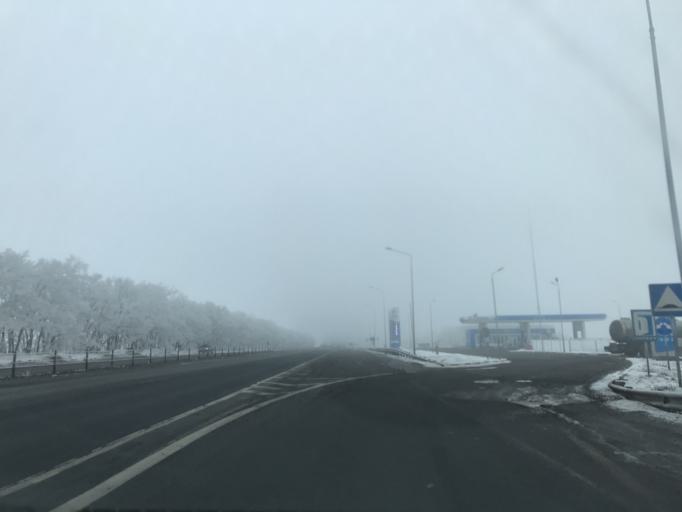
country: RU
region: Rostov
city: Likhoy
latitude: 48.1778
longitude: 40.2648
